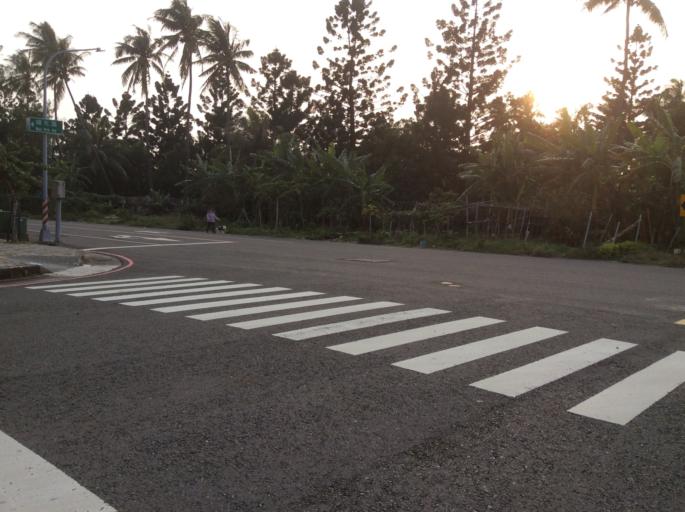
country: TW
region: Kaohsiung
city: Kaohsiung
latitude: 22.6956
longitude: 120.2866
